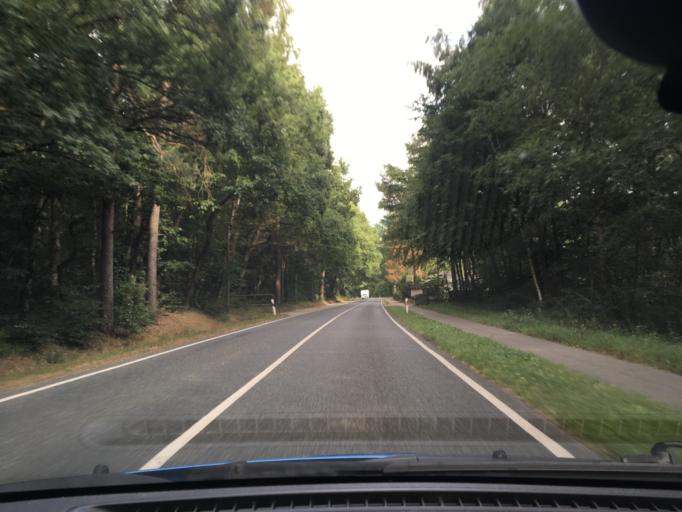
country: DE
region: Lower Saxony
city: Neu Wulmstorf
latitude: 53.4078
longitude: 9.8216
